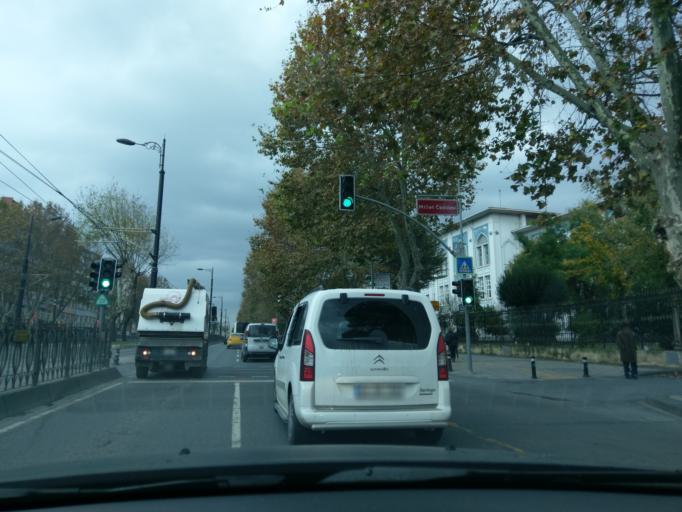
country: TR
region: Istanbul
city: Istanbul
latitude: 41.0138
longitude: 28.9366
